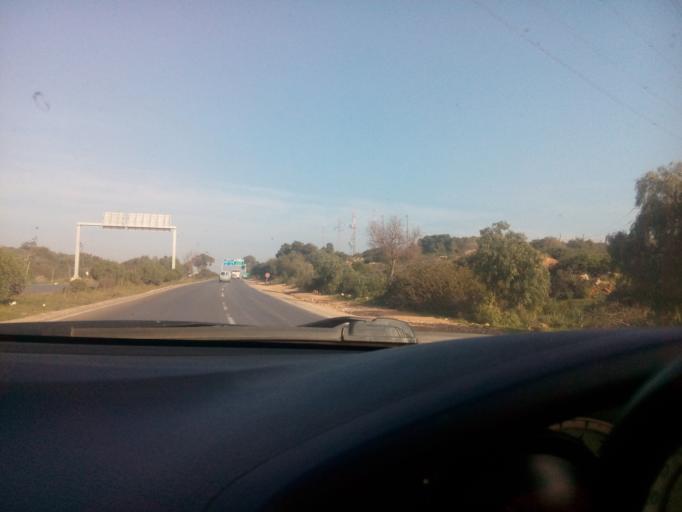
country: DZ
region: Oran
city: Oran
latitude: 35.6431
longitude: -0.7043
